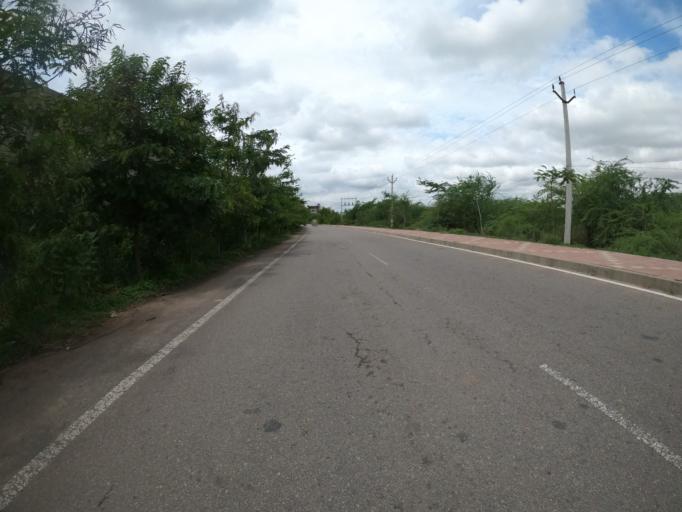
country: IN
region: Telangana
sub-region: Rangareddi
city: Sriramnagar
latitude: 17.2594
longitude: 78.3752
